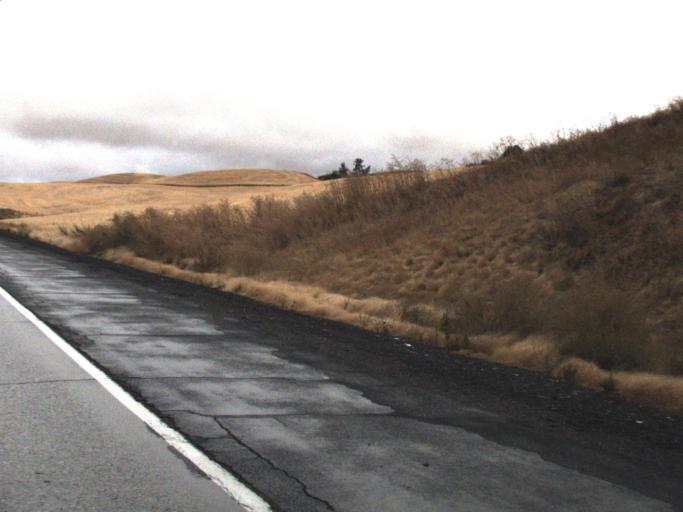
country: US
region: Washington
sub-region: Whitman County
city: Colfax
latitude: 47.1022
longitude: -117.3789
